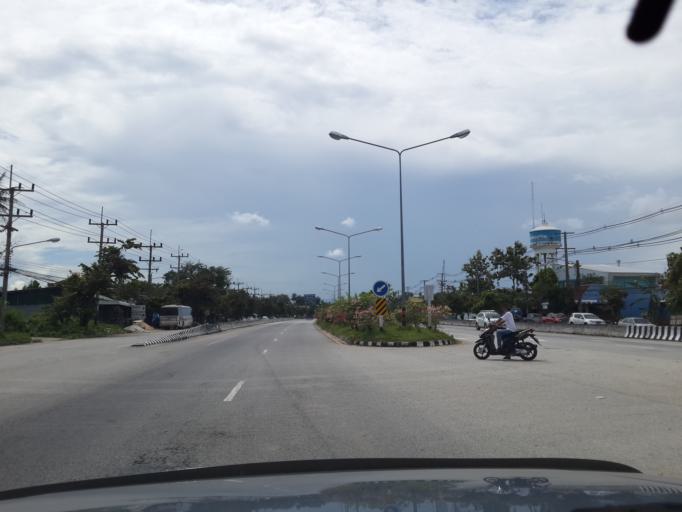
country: TH
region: Narathiwat
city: Narathiwat
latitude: 6.4123
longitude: 101.8066
